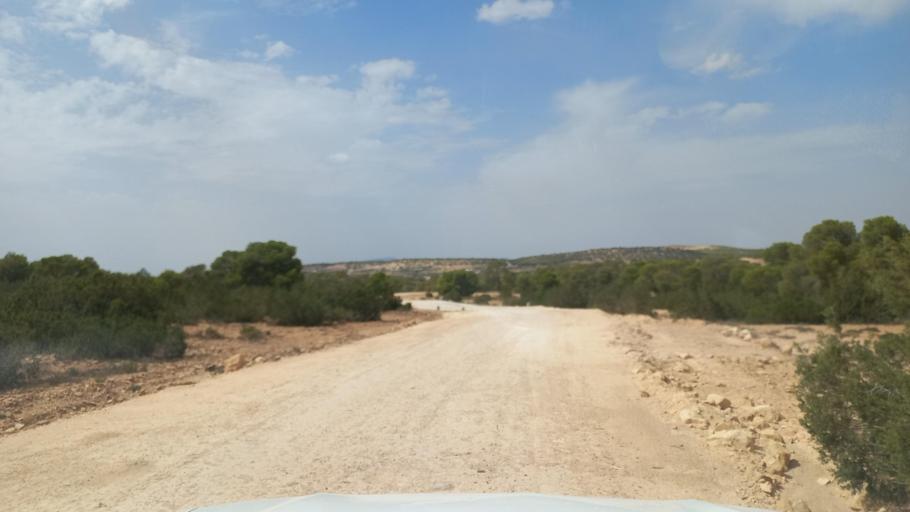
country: TN
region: Al Qasrayn
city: Kasserine
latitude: 35.3821
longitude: 8.8771
